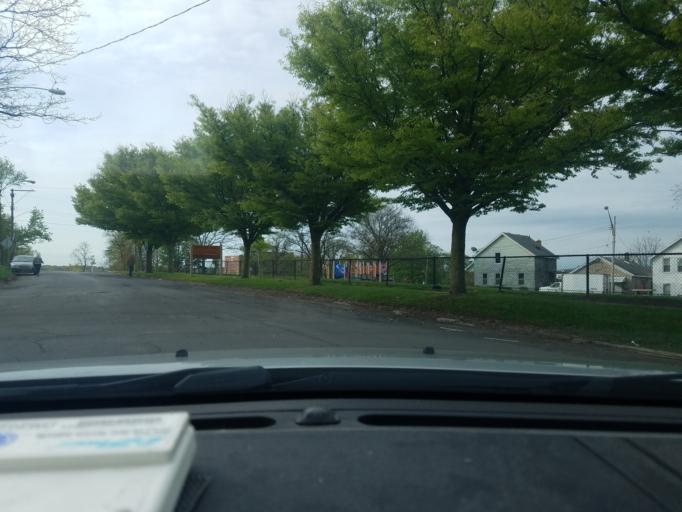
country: US
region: New York
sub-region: Onondaga County
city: Syracuse
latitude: 43.0604
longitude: -76.1413
